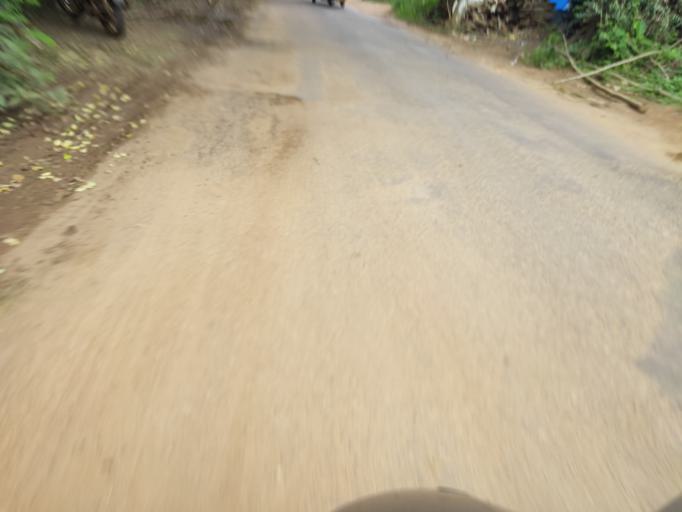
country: IN
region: Kerala
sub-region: Malappuram
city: Manjeri
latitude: 11.2424
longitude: 76.2871
